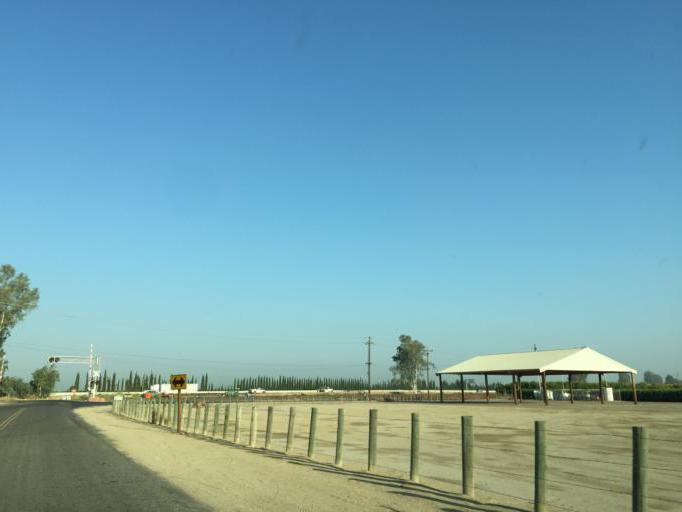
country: US
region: California
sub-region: Tulare County
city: London
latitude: 36.4592
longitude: -119.4909
